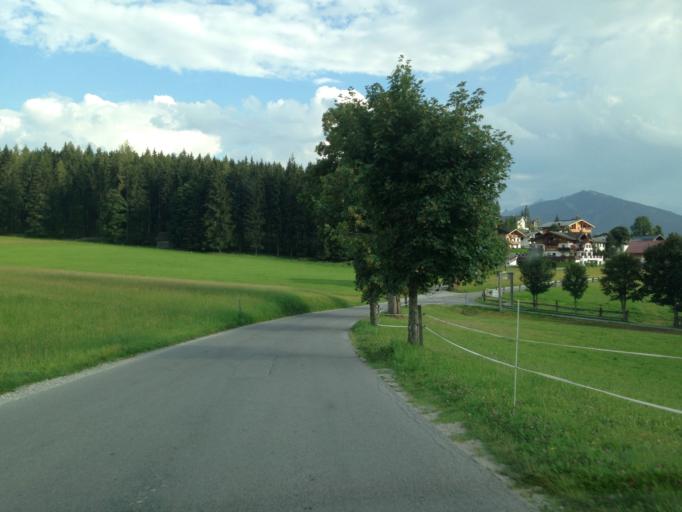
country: AT
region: Styria
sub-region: Politischer Bezirk Liezen
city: Schladming
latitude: 47.4171
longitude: 13.6378
